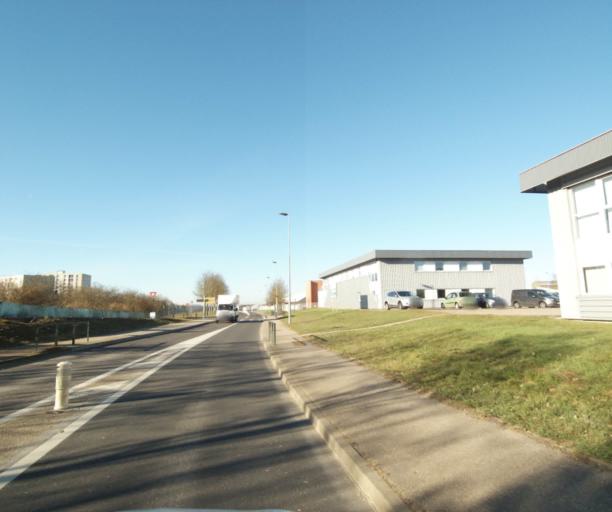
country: FR
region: Lorraine
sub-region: Departement de Meurthe-et-Moselle
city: Laxou
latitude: 48.7033
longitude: 6.1303
